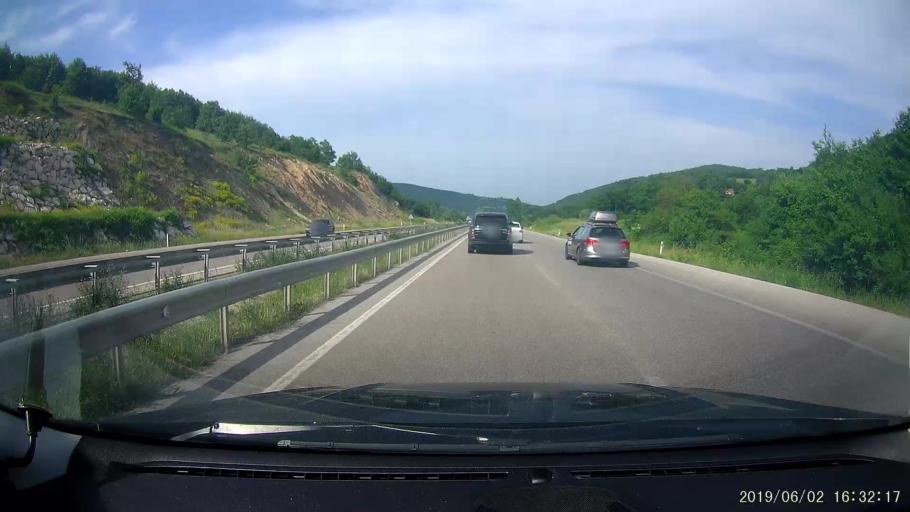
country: TR
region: Samsun
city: Ladik
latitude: 41.0382
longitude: 35.9176
